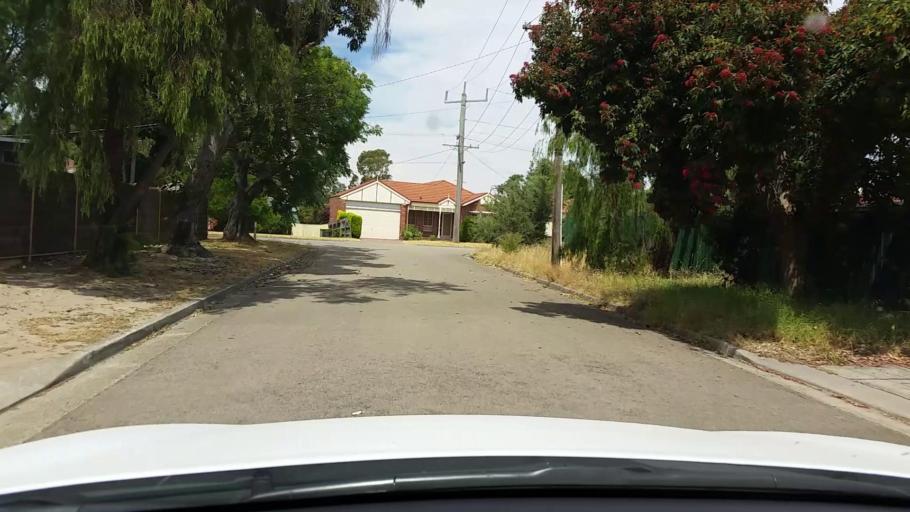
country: AU
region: Victoria
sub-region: Mornington Peninsula
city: Rosebud West
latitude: -38.3691
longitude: 144.8907
